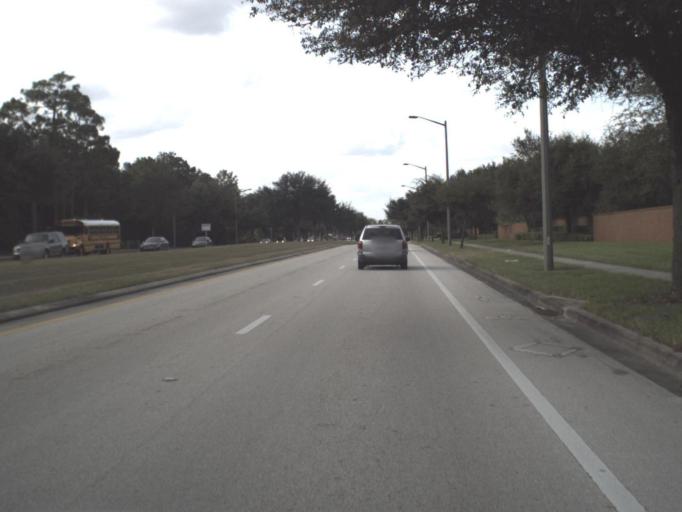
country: US
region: Florida
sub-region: Orange County
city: Conway
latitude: 28.4208
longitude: -81.2461
